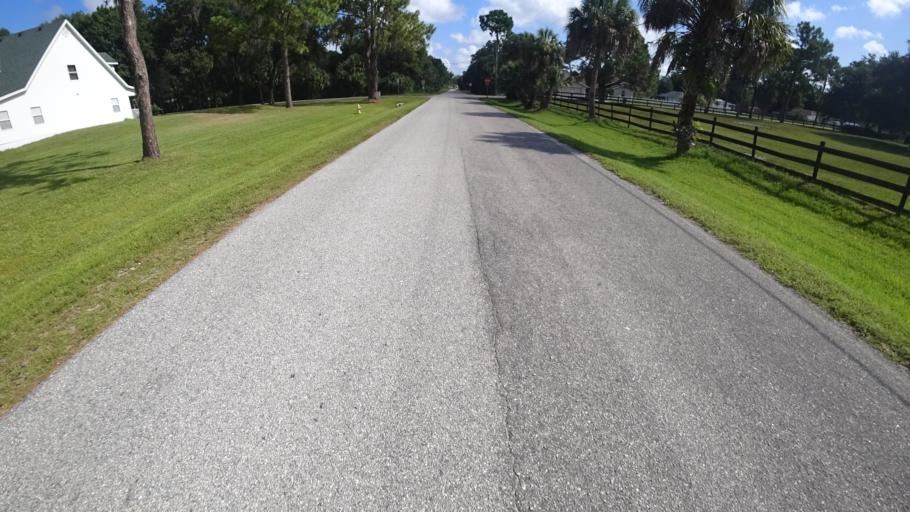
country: US
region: Florida
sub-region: Manatee County
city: Ellenton
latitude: 27.4869
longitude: -82.4794
